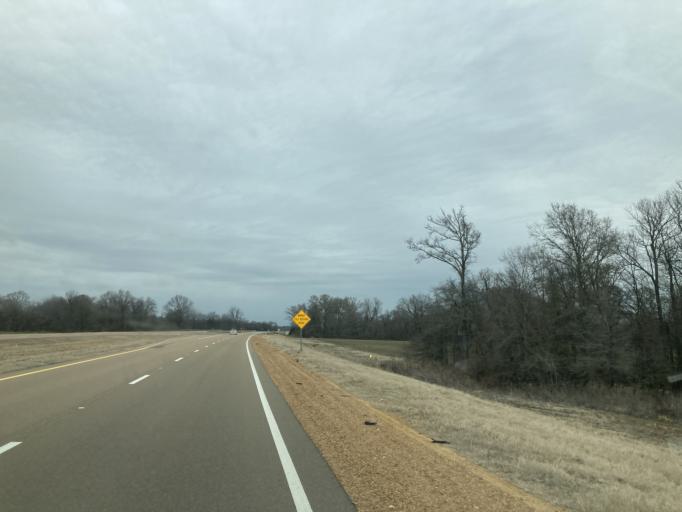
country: US
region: Mississippi
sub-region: Yazoo County
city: Yazoo City
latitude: 32.9960
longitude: -90.4694
